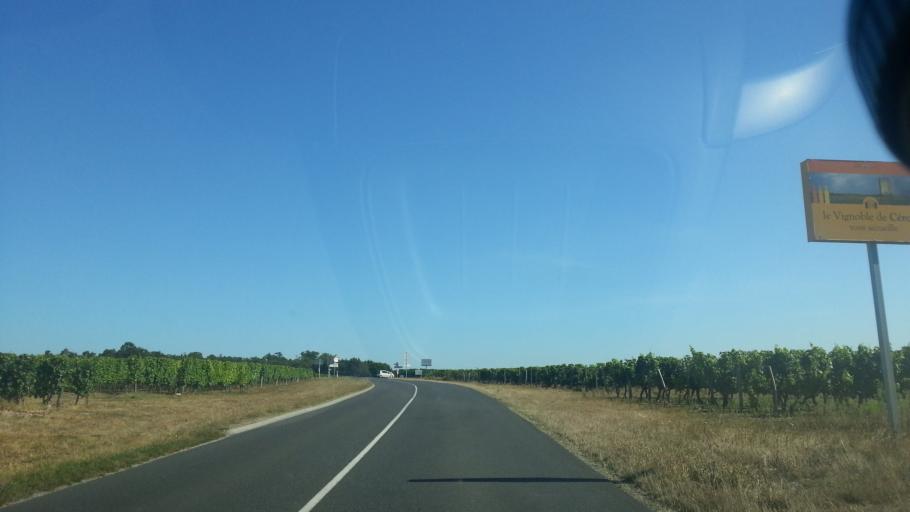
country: FR
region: Aquitaine
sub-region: Departement de la Gironde
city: Illats
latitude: 44.6247
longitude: -0.3696
